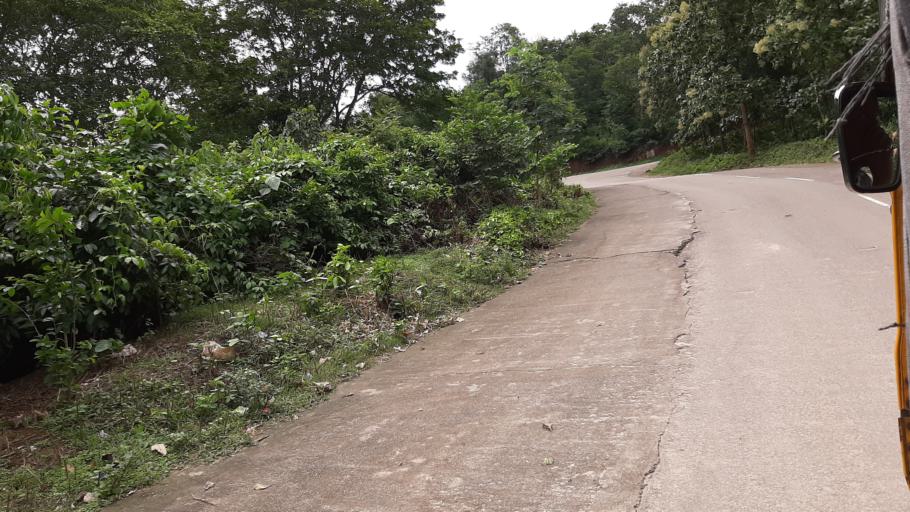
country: IN
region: Andhra Pradesh
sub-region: Vizianagaram District
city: Salur
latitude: 18.2763
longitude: 83.0376
